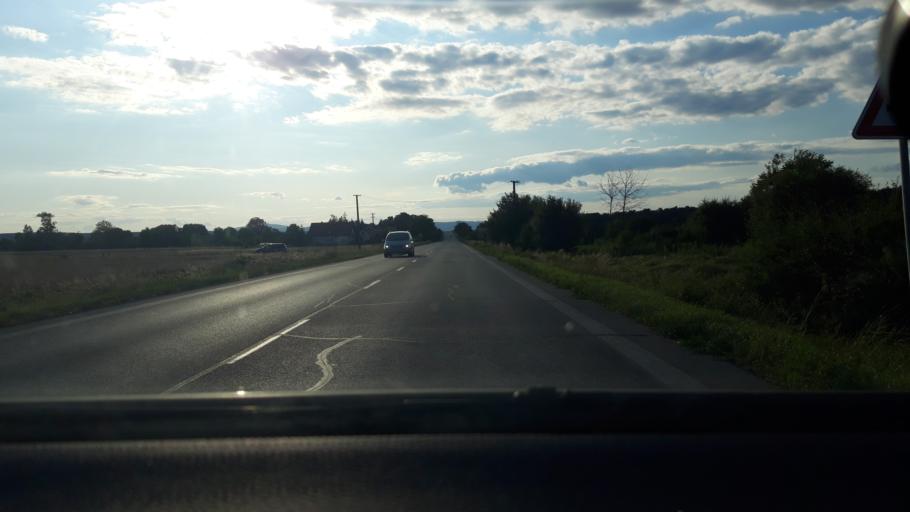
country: SK
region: Banskobystricky
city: Lucenec
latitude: 48.3040
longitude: 19.7268
